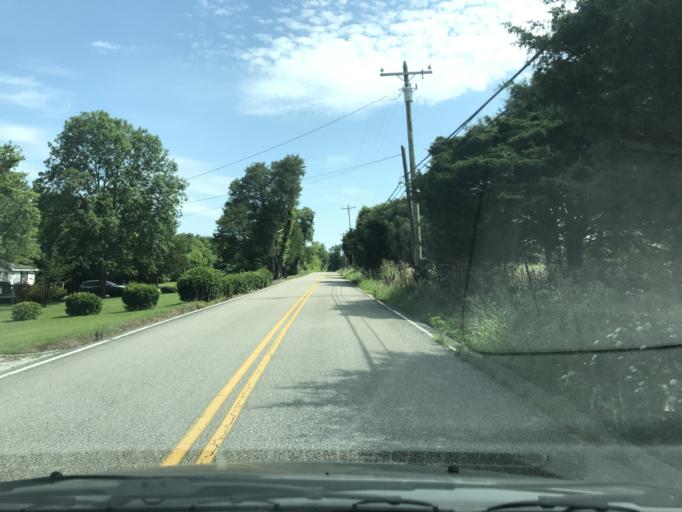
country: US
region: Tennessee
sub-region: Hamilton County
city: Lakesite
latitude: 35.2062
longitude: -85.0238
